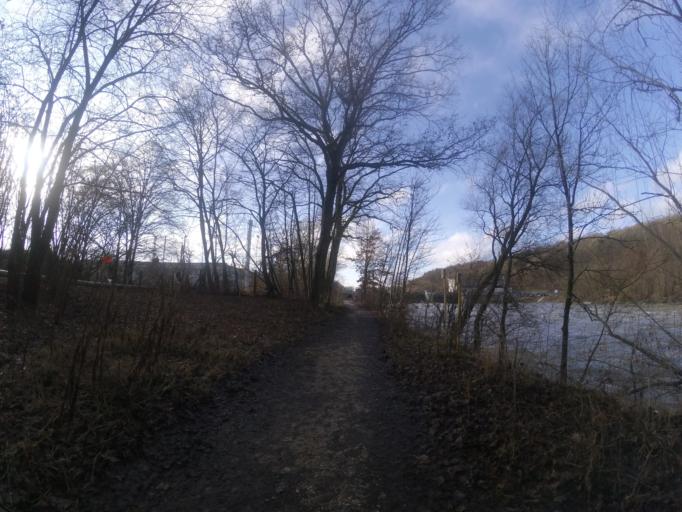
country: DE
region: Bavaria
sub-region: Swabia
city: Neu-Ulm
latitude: 48.4244
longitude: 10.0288
